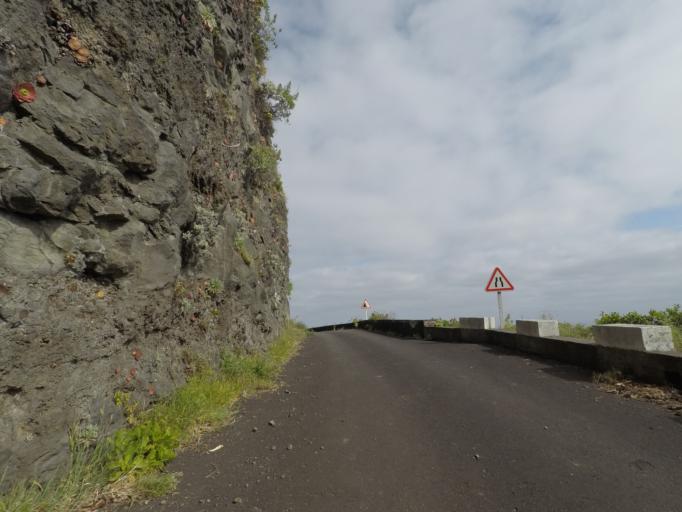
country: PT
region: Madeira
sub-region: Sao Vicente
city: Sao Vicente
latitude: 32.8122
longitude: -17.0659
